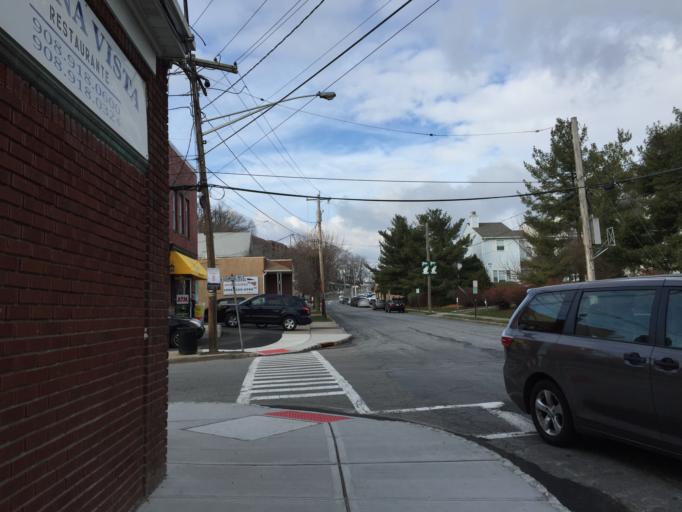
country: US
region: New Jersey
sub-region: Union County
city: Summit
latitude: 40.7129
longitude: -74.3485
